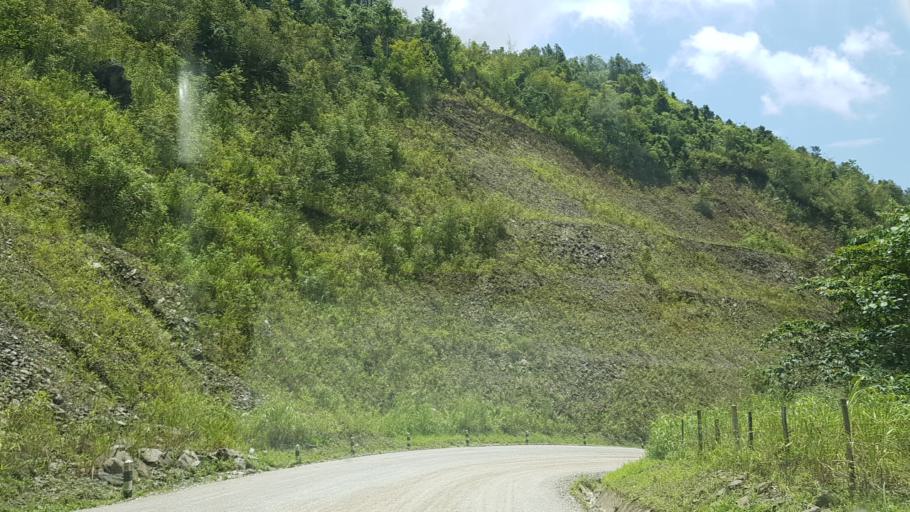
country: LA
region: Vientiane
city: Muang Kasi
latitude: 19.3871
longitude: 102.1504
